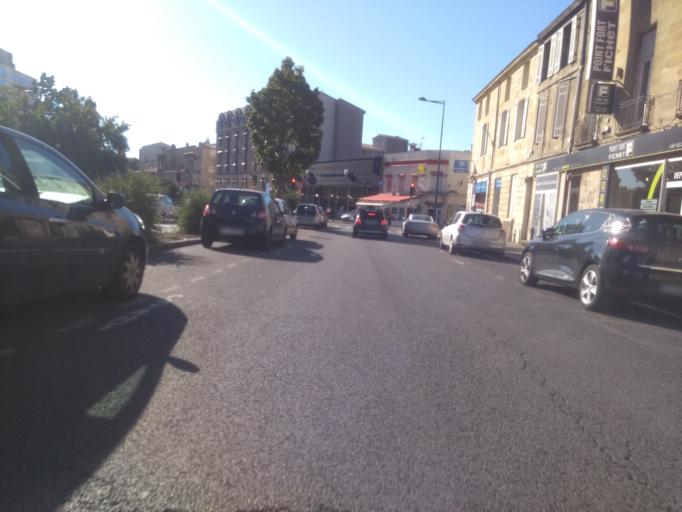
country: FR
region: Aquitaine
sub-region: Departement de la Gironde
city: Bordeaux
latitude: 44.8400
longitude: -0.5856
